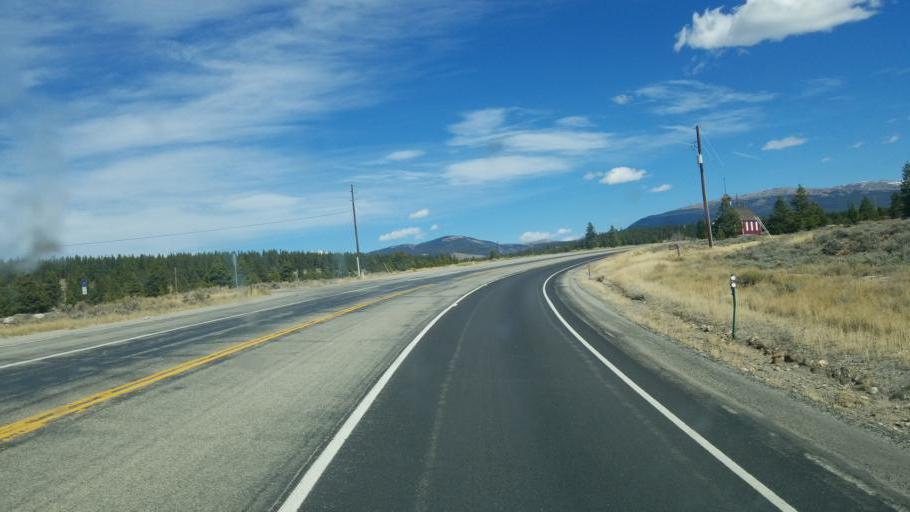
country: US
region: Colorado
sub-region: Lake County
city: Leadville North
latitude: 39.2230
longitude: -106.3482
